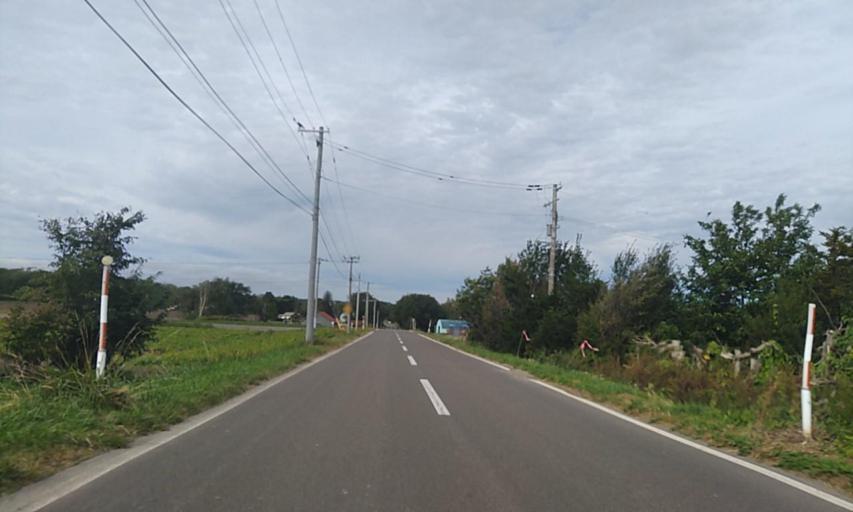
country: JP
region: Hokkaido
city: Abashiri
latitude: 43.7957
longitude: 144.5597
